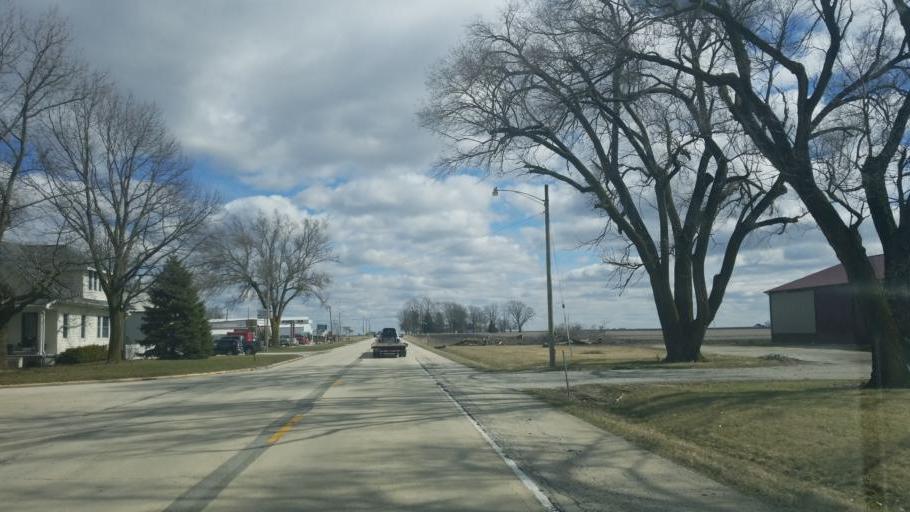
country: US
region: Illinois
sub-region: Moultrie County
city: Lovington
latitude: 39.7922
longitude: -88.5924
